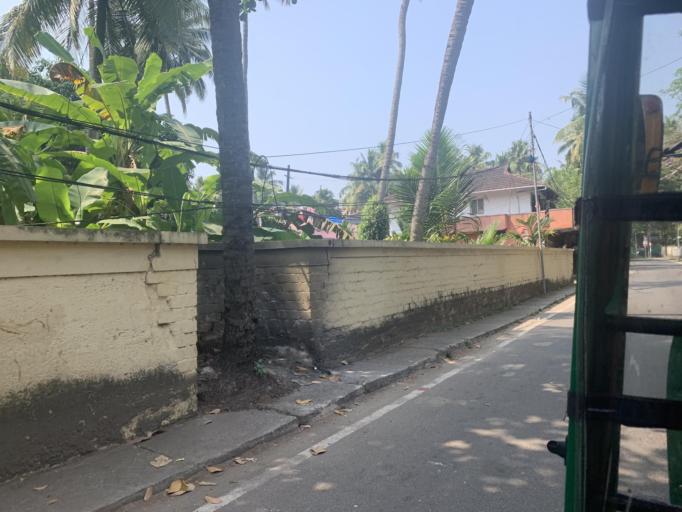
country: IN
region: Kerala
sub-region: Ernakulam
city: Cochin
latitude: 9.9417
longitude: 76.3014
